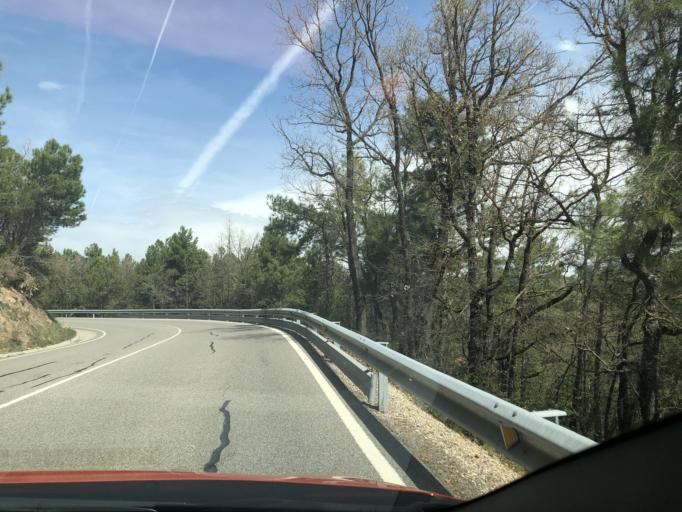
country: ES
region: Catalonia
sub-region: Provincia de Lleida
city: Solsona
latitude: 42.0379
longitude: 1.5162
